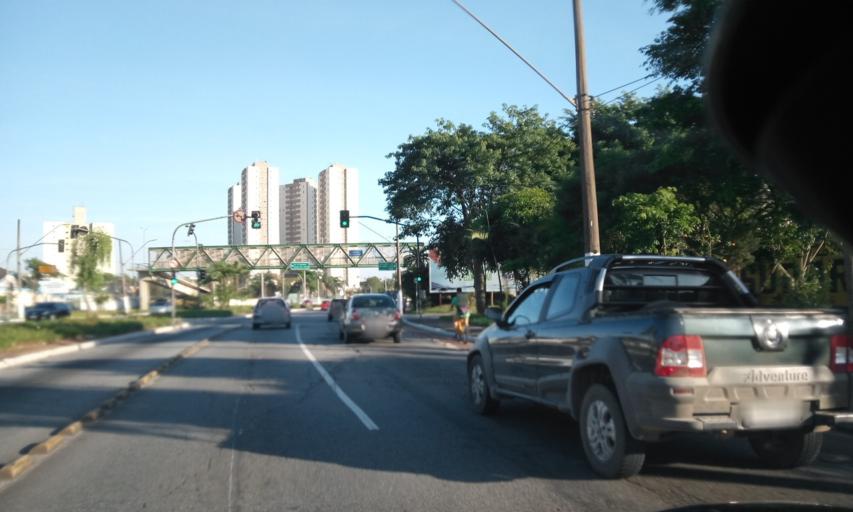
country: BR
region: Sao Paulo
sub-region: Santo Andre
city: Santo Andre
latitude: -23.6680
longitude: -46.5114
